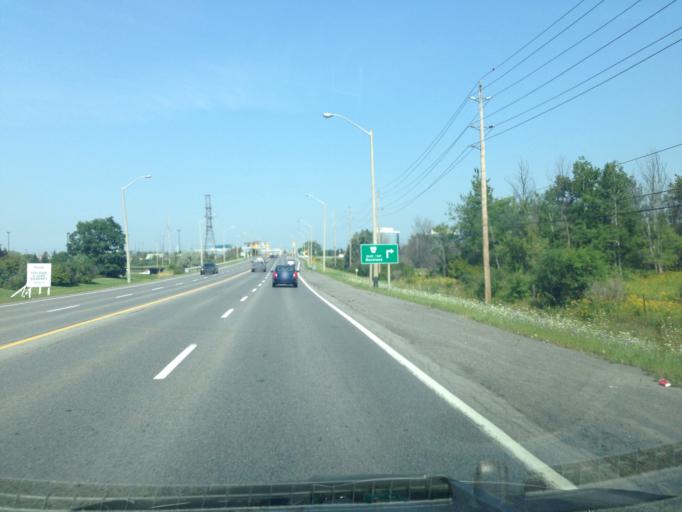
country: CA
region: Ontario
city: Ottawa
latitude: 45.4283
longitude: -75.6016
